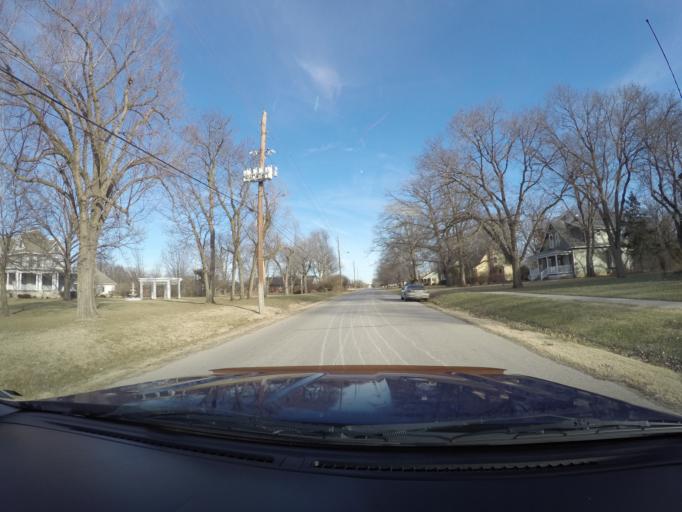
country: US
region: Kansas
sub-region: Harvey County
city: North Newton
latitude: 38.0718
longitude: -97.3423
